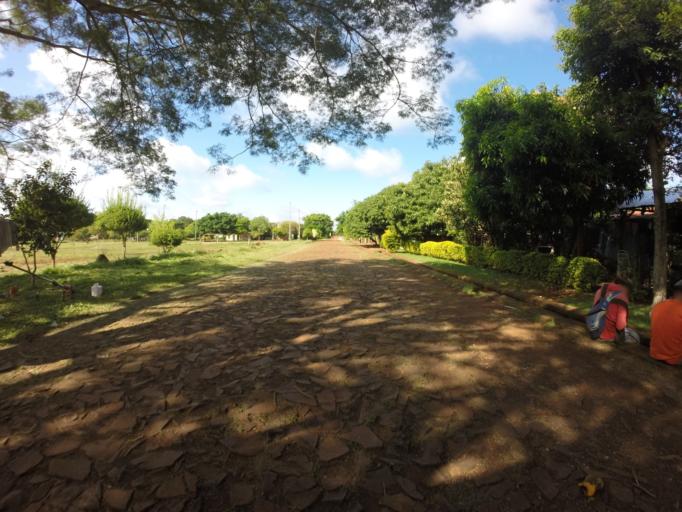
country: PY
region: Alto Parana
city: Ciudad del Este
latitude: -25.3966
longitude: -54.6433
